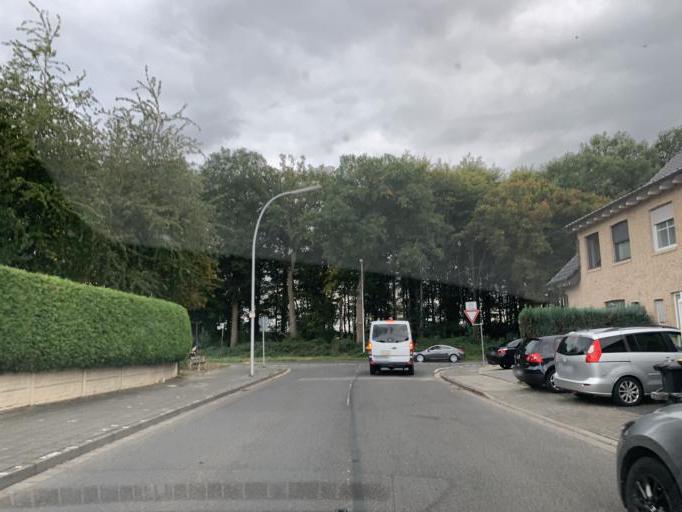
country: DE
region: North Rhine-Westphalia
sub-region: Regierungsbezirk Koln
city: Wassenberg
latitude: 51.0542
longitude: 6.1600
